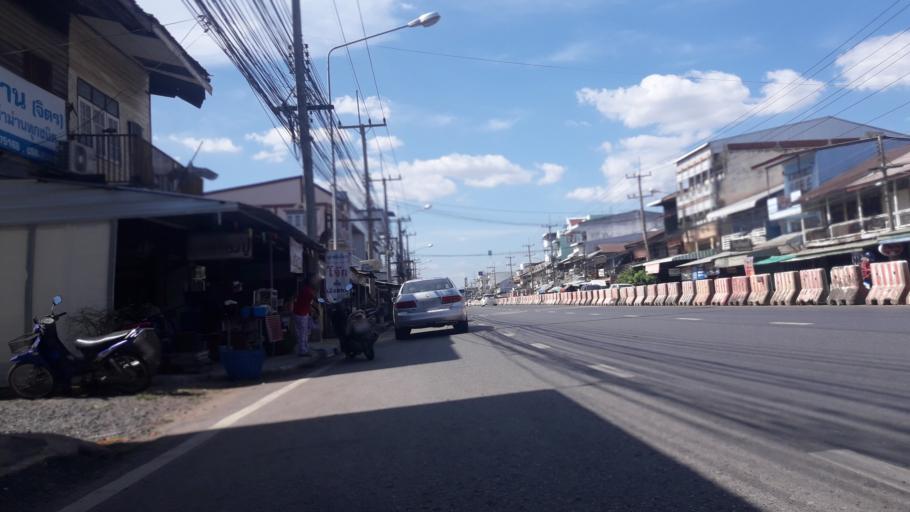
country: TH
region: Phichit
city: Thap Khlo
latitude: 16.1675
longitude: 100.5795
